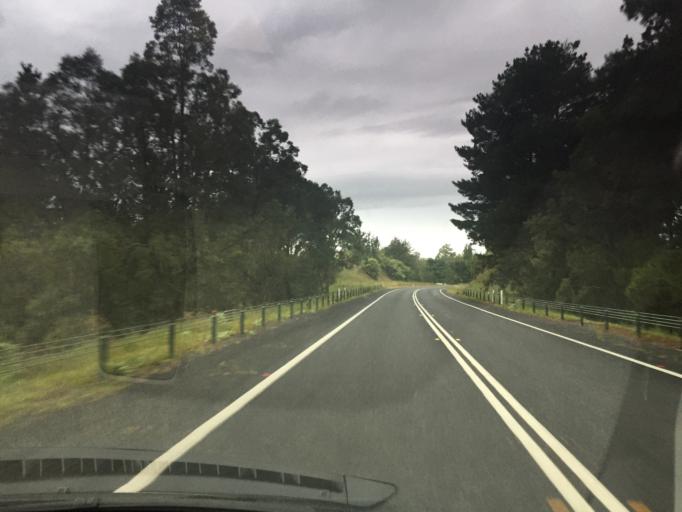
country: AU
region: New South Wales
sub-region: Bega Valley
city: Bega
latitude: -36.6392
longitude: 149.5800
